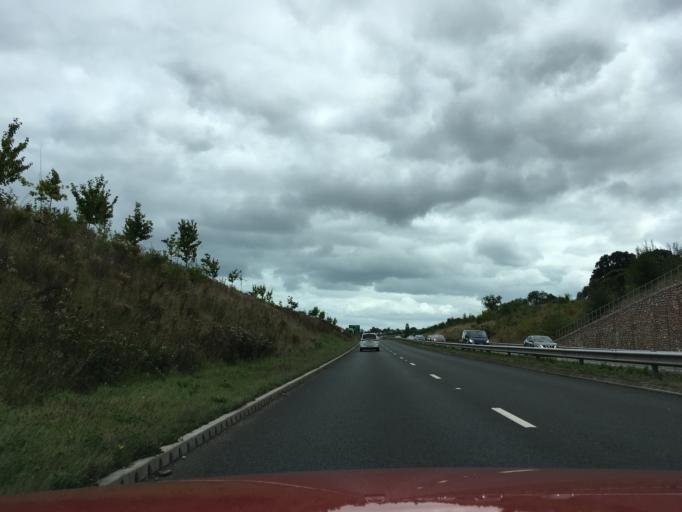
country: GB
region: England
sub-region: Devon
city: Kingskerswell
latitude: 50.4946
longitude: -3.5846
